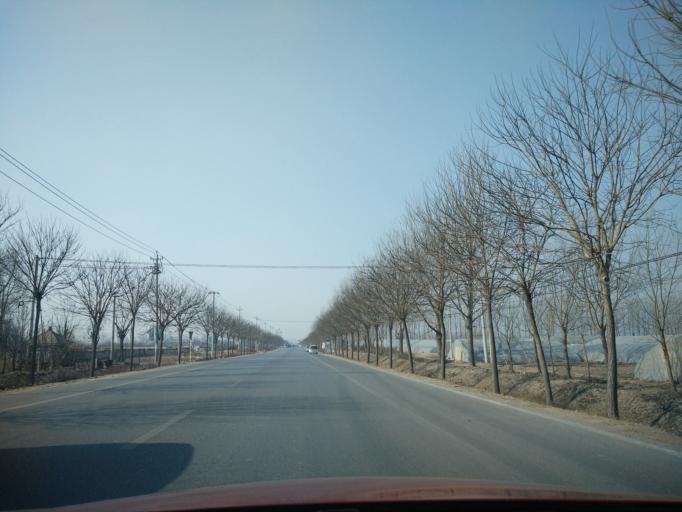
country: CN
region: Beijing
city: Yinghai
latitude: 39.7059
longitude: 116.4409
